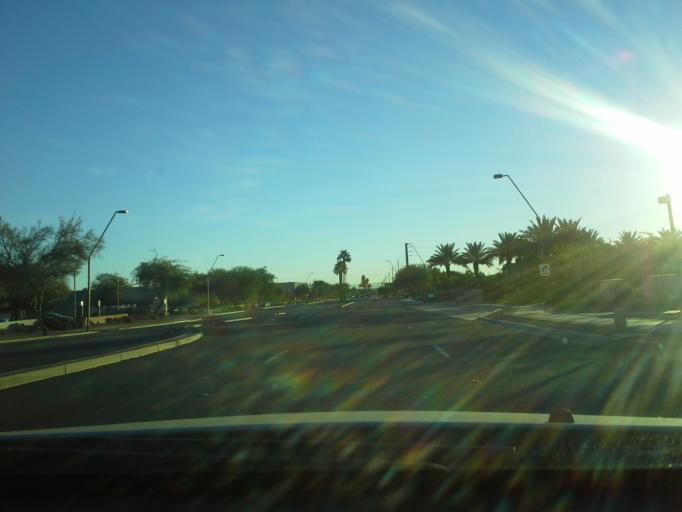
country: US
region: Arizona
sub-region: Maricopa County
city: Guadalupe
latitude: 33.3491
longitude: -111.9577
